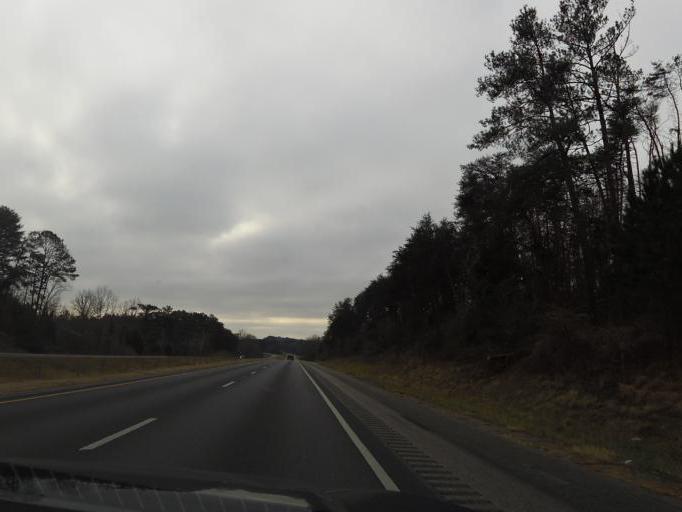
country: US
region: Alabama
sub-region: Chilton County
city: Jemison
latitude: 33.0200
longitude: -86.7156
